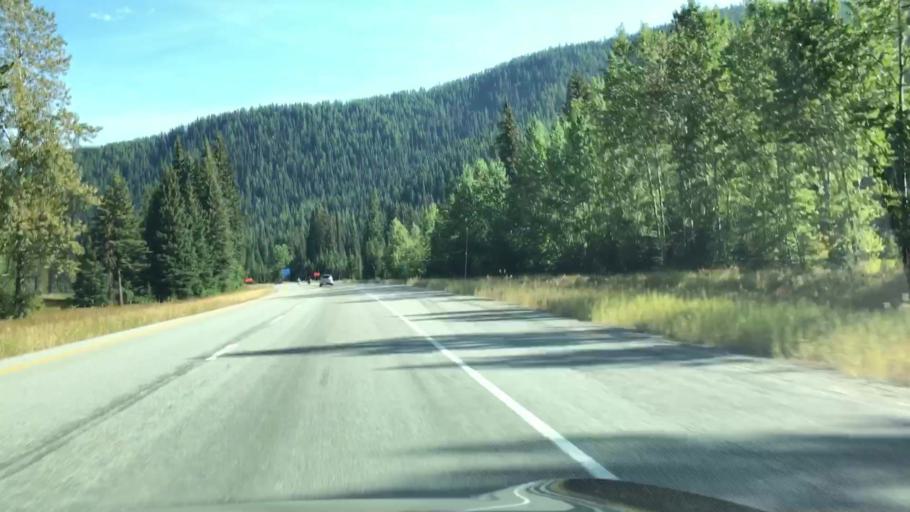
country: US
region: Idaho
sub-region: Shoshone County
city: Wallace
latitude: 47.4260
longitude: -115.6384
